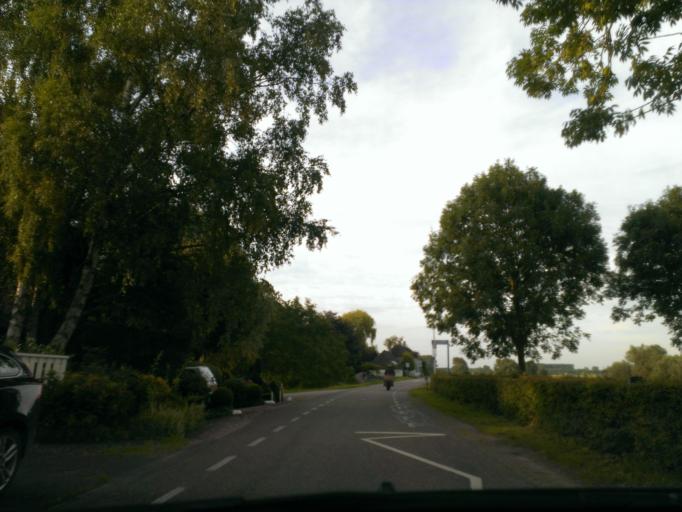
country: NL
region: Overijssel
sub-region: Gemeente Olst-Wijhe
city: Olst
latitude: 52.3359
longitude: 6.0927
